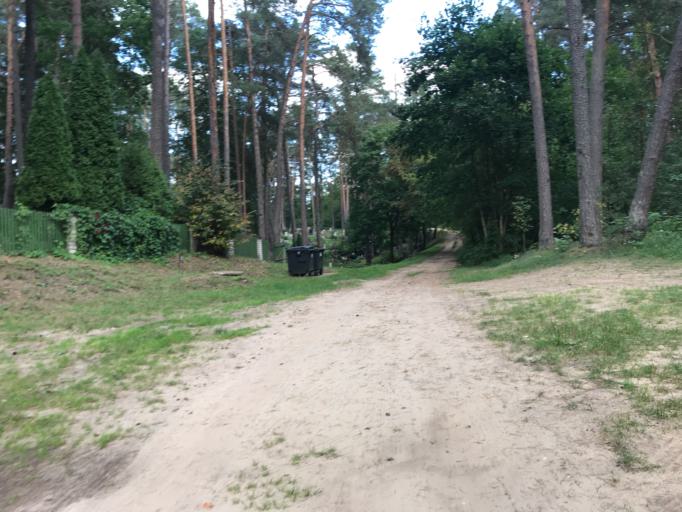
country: LT
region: Alytaus apskritis
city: Druskininkai
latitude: 54.0121
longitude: 23.9713
